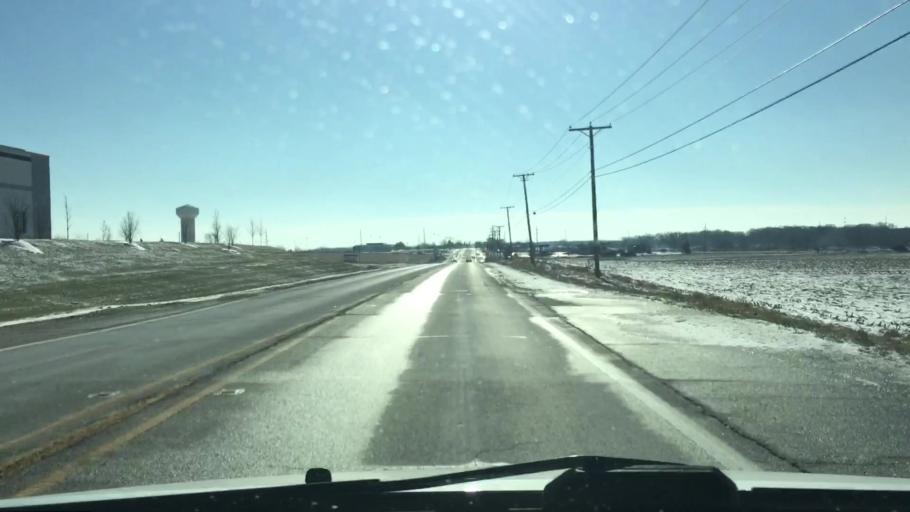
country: US
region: Illinois
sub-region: Kane County
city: South Elgin
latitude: 41.9985
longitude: -88.2684
